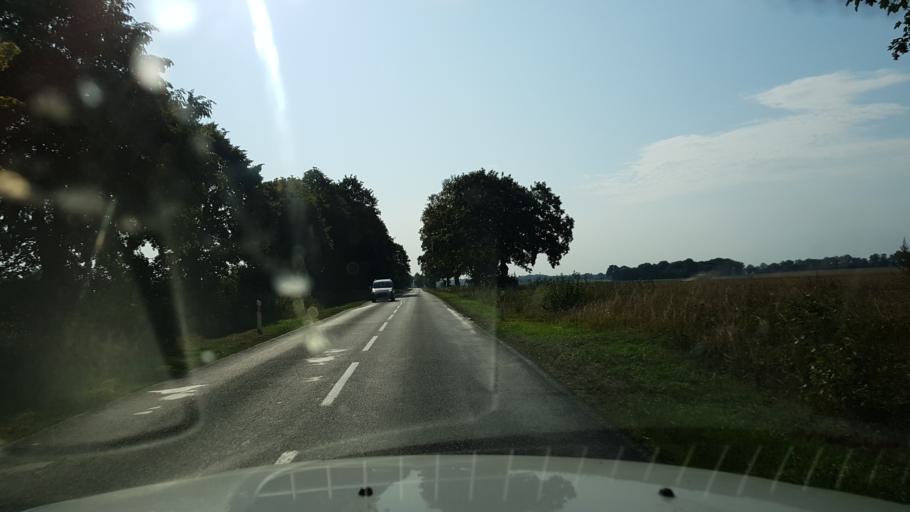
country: PL
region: West Pomeranian Voivodeship
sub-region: Powiat gryficki
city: Ploty
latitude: 53.7957
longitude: 15.2795
